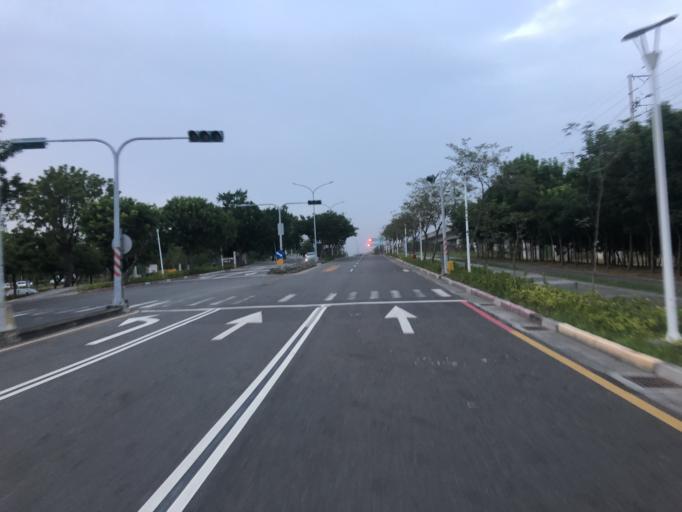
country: TW
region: Taiwan
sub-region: Tainan
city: Tainan
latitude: 23.0888
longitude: 120.2864
